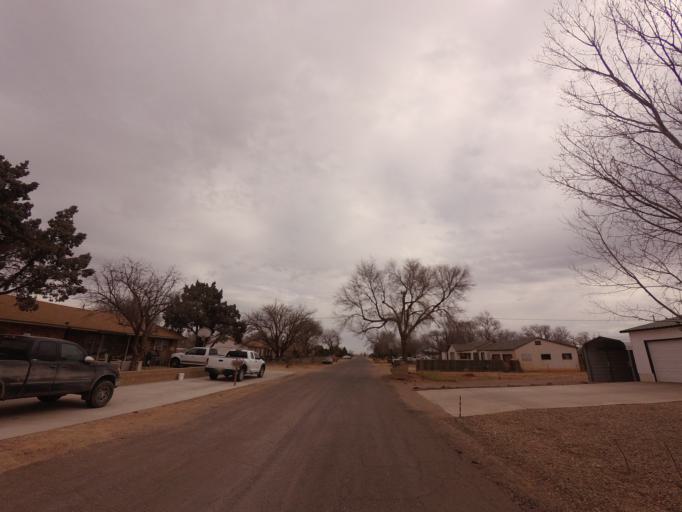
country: US
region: New Mexico
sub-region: Curry County
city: Clovis
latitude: 34.3775
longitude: -103.2004
